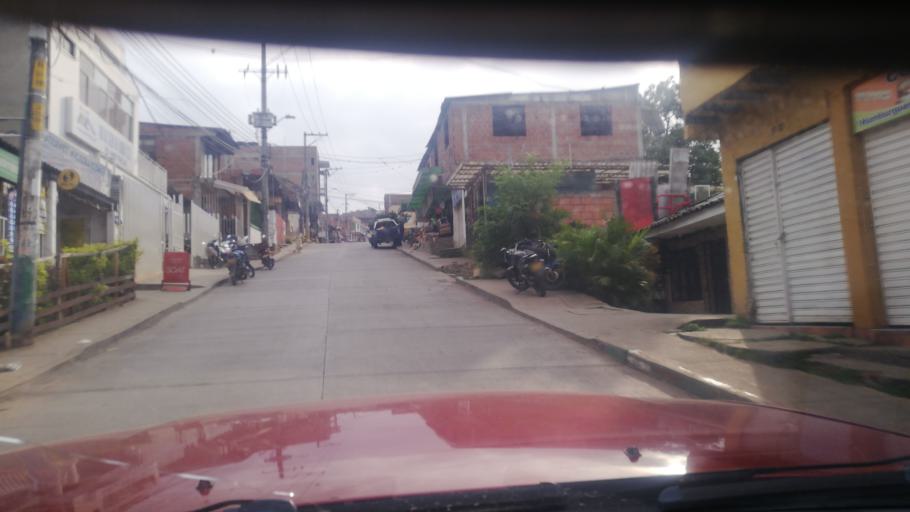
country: CO
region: Valle del Cauca
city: Cali
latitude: 3.4840
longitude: -76.5528
